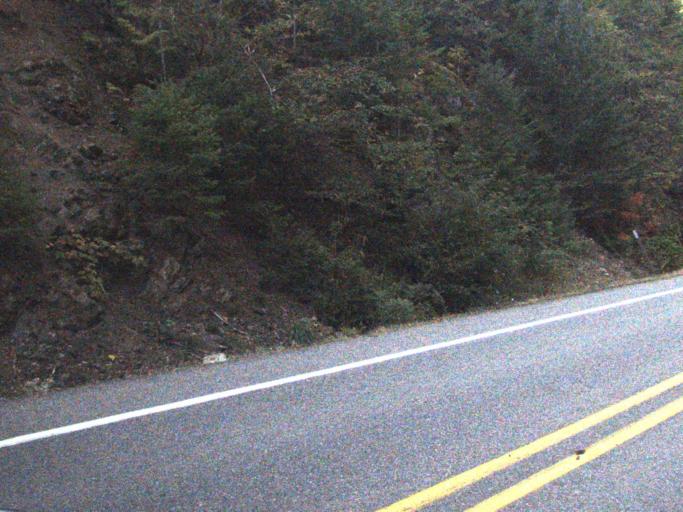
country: US
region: Washington
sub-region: Snohomish County
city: Darrington
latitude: 48.7052
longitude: -120.9145
